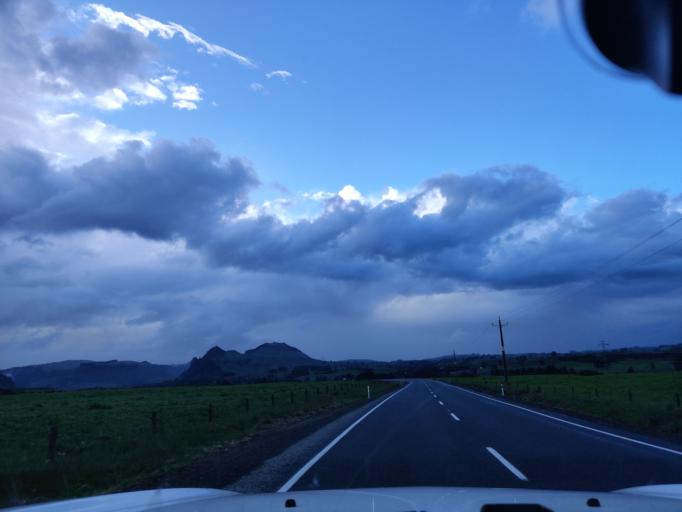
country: NZ
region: Waikato
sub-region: South Waikato District
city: Tokoroa
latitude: -38.4006
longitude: 175.7892
